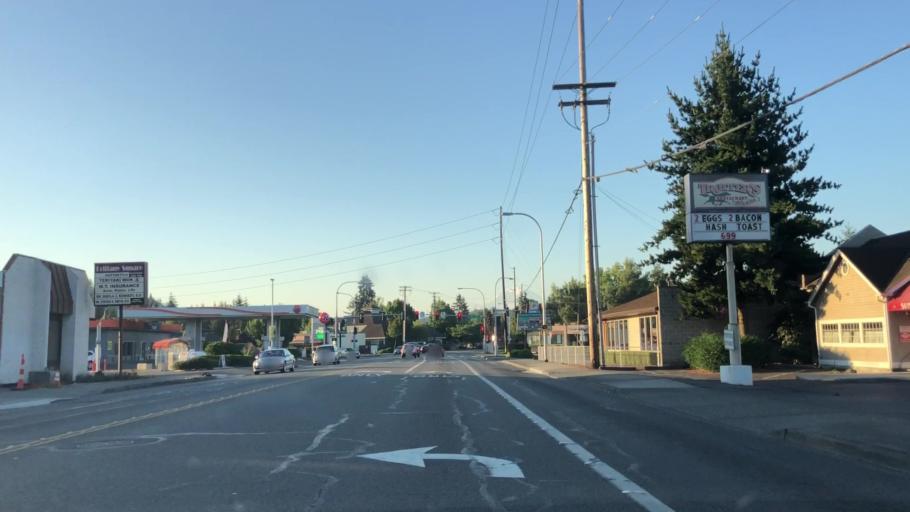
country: US
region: Washington
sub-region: King County
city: Auburn
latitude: 47.3159
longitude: -122.2152
